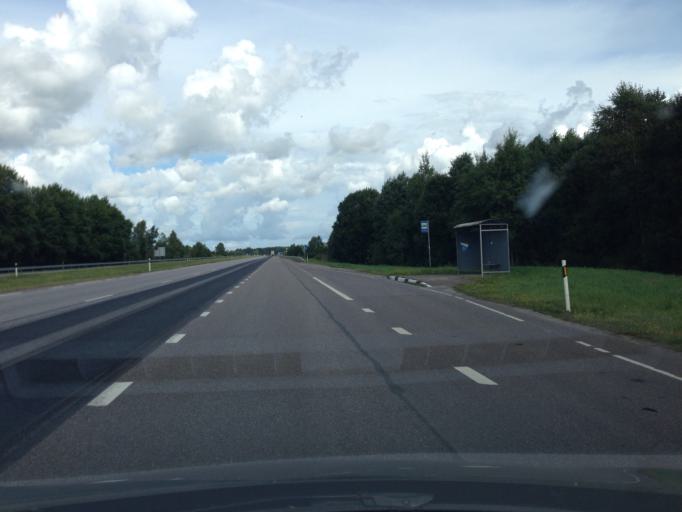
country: EE
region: Harju
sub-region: Saue linn
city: Saue
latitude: 59.2682
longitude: 24.5170
